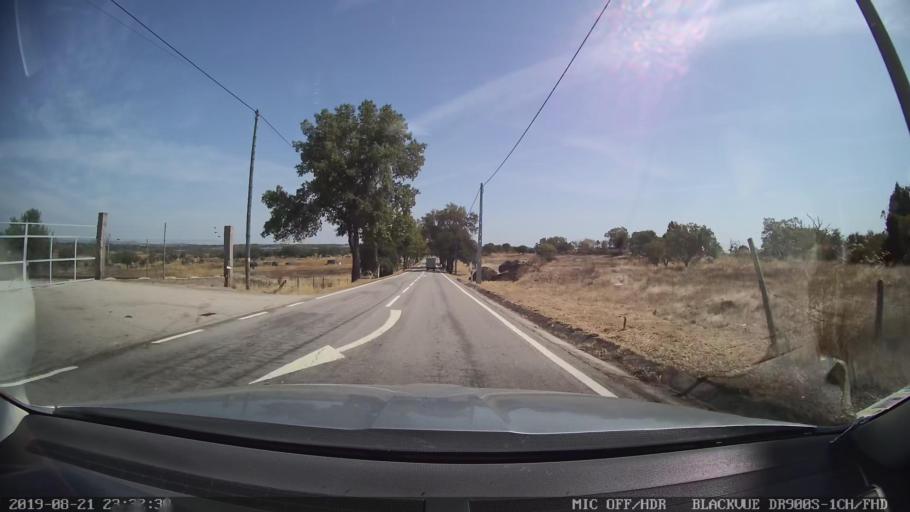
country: PT
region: Guarda
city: Alcains
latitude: 39.8790
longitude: -7.4121
